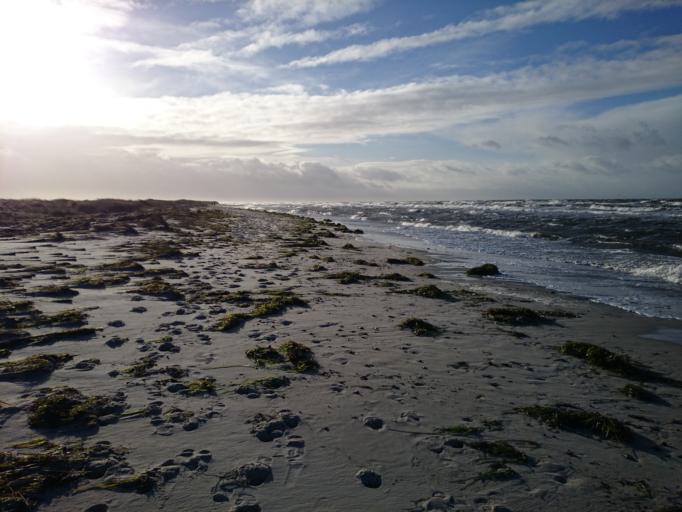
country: SE
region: Skane
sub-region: Vellinge Kommun
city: Skanor med Falsterbo
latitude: 55.3840
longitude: 12.8120
